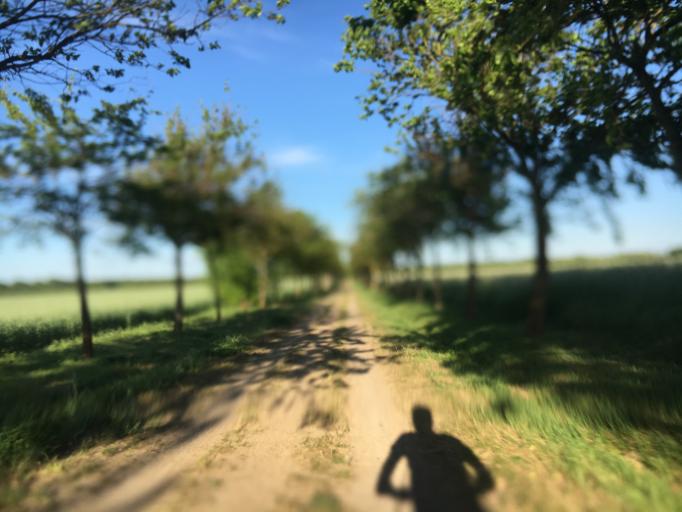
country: DE
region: Brandenburg
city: Potsdam
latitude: 52.4306
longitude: 13.0255
